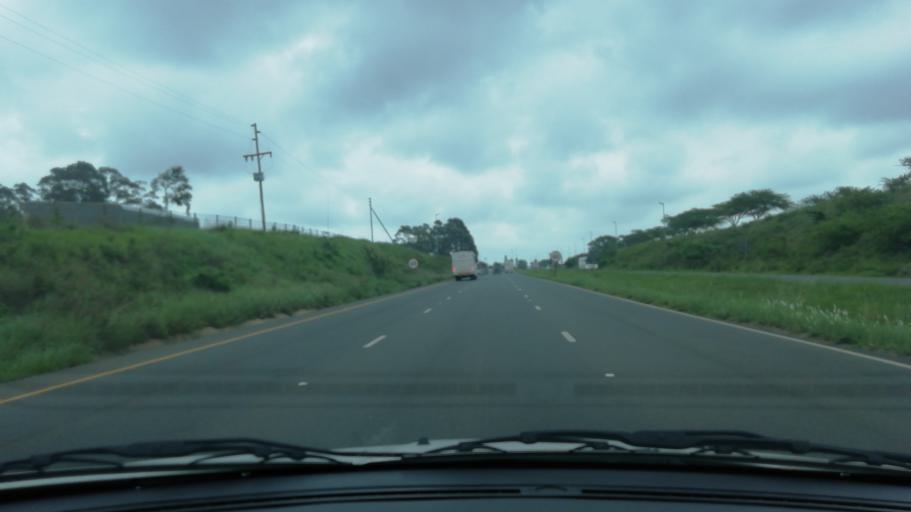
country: ZA
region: KwaZulu-Natal
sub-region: uThungulu District Municipality
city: Empangeni
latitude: -28.7669
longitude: 31.9180
